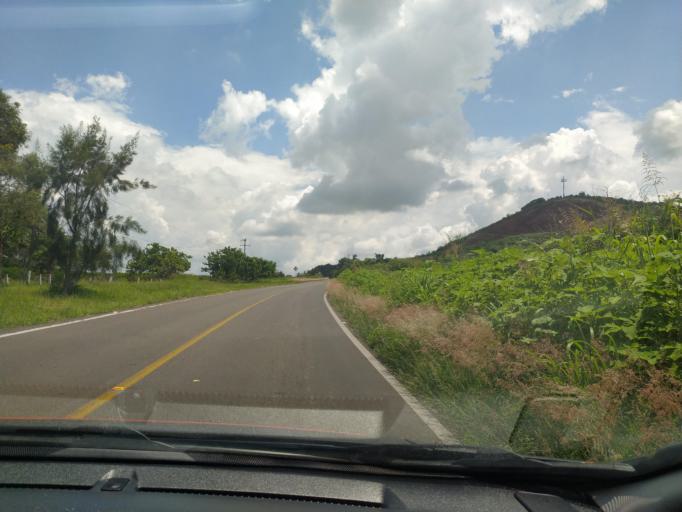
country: MX
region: Jalisco
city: Villa Corona
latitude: 20.4002
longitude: -103.6802
